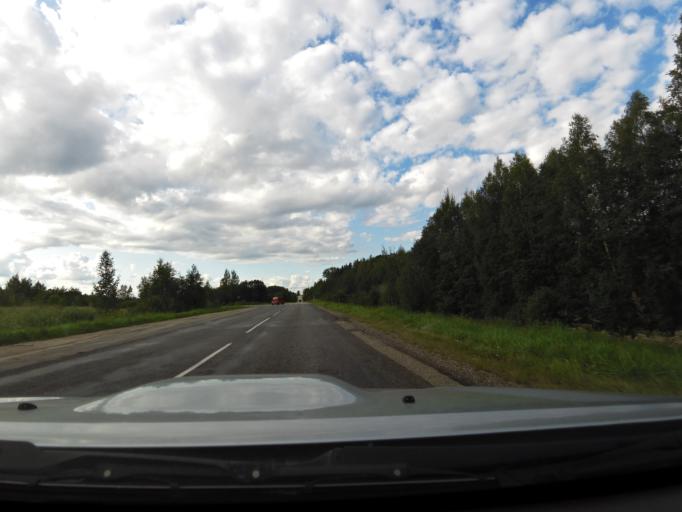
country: LV
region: Akniste
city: Akniste
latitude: 56.0217
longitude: 25.9210
